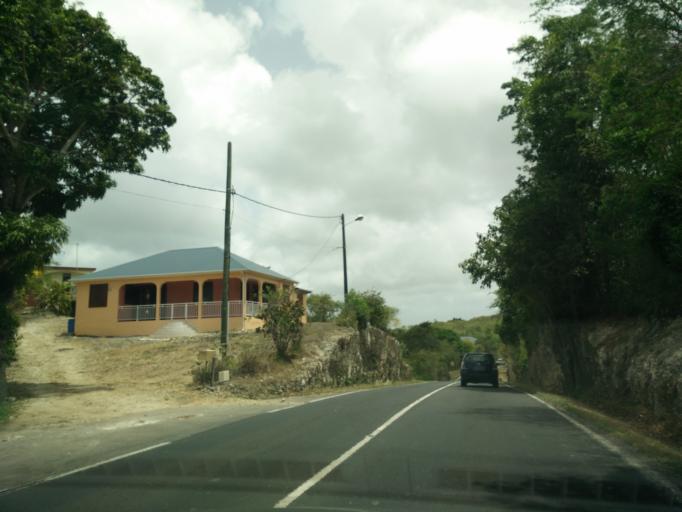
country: GP
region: Guadeloupe
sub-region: Guadeloupe
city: Petit-Canal
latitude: 16.3632
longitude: -61.4569
